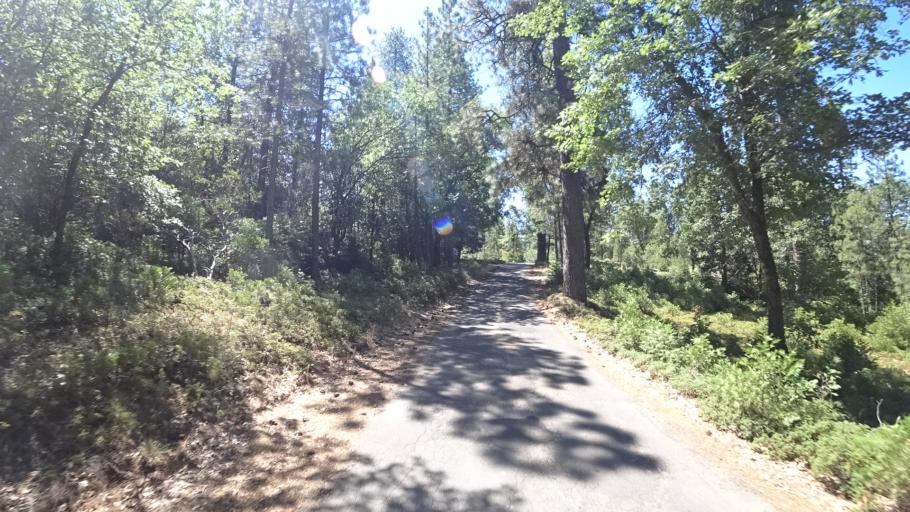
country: US
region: California
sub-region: Amador County
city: Pioneer
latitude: 38.4184
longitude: -120.4950
